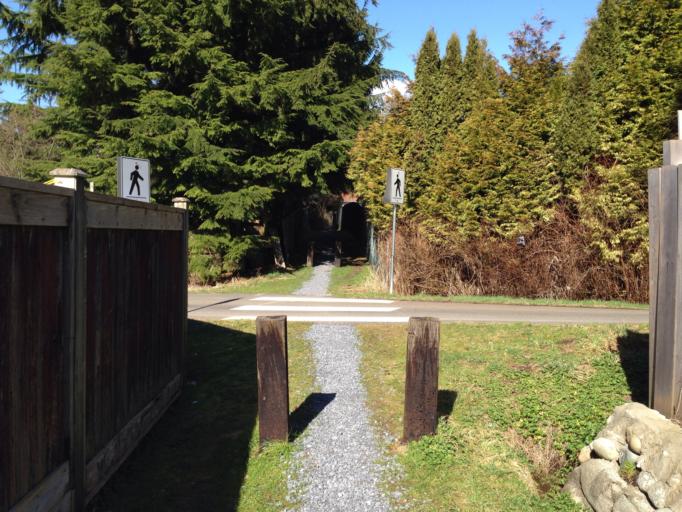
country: CA
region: British Columbia
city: Port Moody
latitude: 49.2676
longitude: -122.8878
